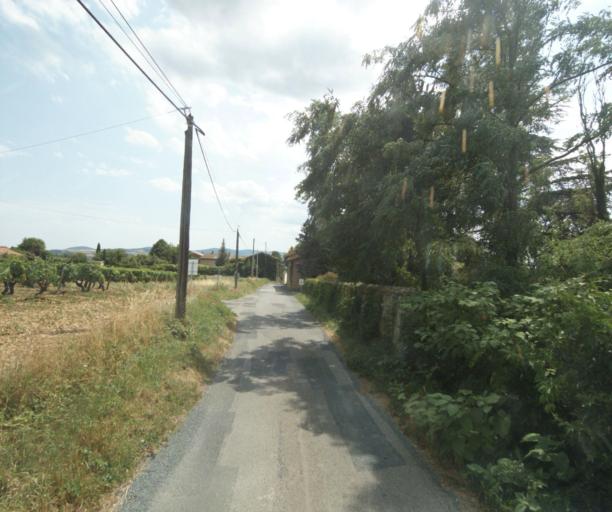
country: FR
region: Rhone-Alpes
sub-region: Departement du Rhone
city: Saint-Germain-Nuelles
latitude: 45.8610
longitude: 4.5995
